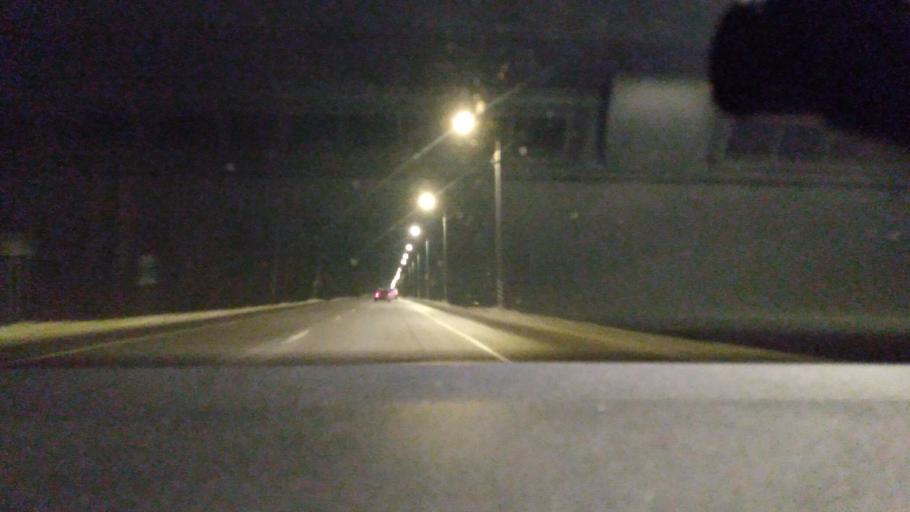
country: RU
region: Moskovskaya
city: Il'inskiy Pogost
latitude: 55.4605
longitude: 38.9836
